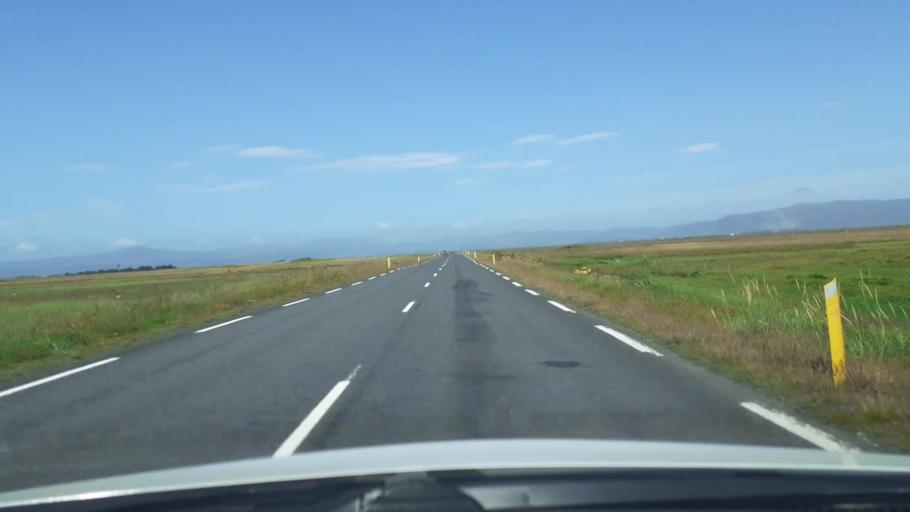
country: IS
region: South
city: Selfoss
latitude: 63.8481
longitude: -21.0955
